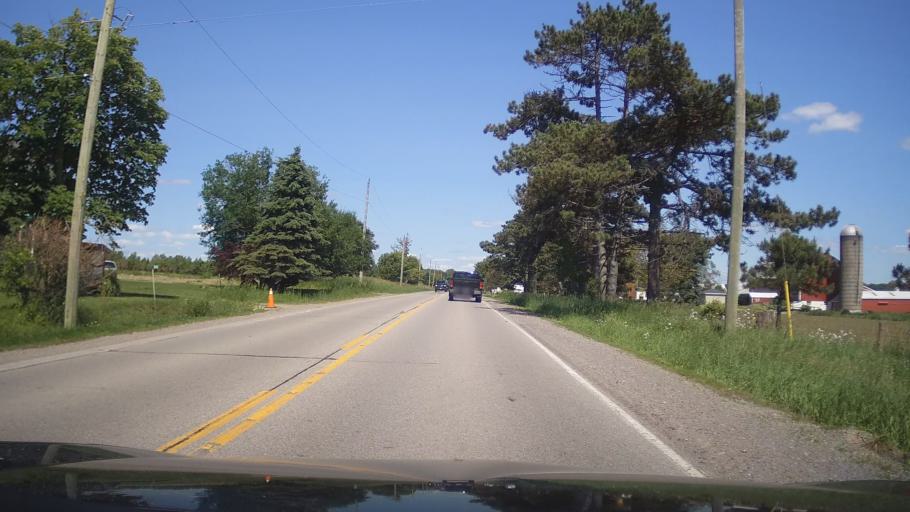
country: CA
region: Ontario
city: Oshawa
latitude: 44.0026
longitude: -78.8246
